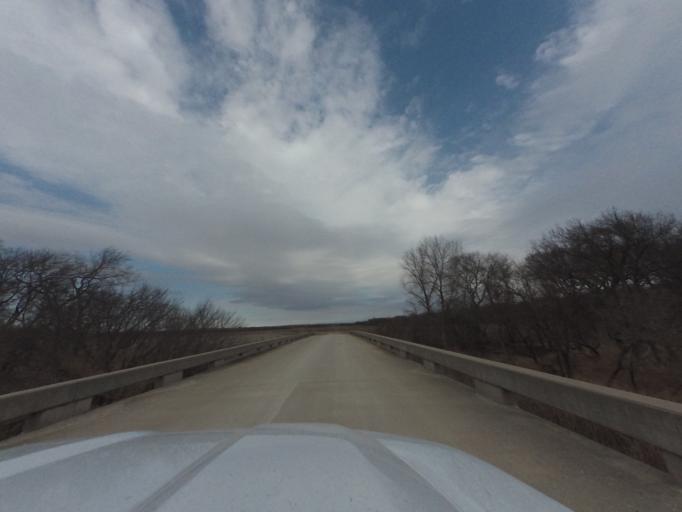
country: US
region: Kansas
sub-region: Chase County
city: Cottonwood Falls
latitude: 38.2943
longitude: -96.7321
